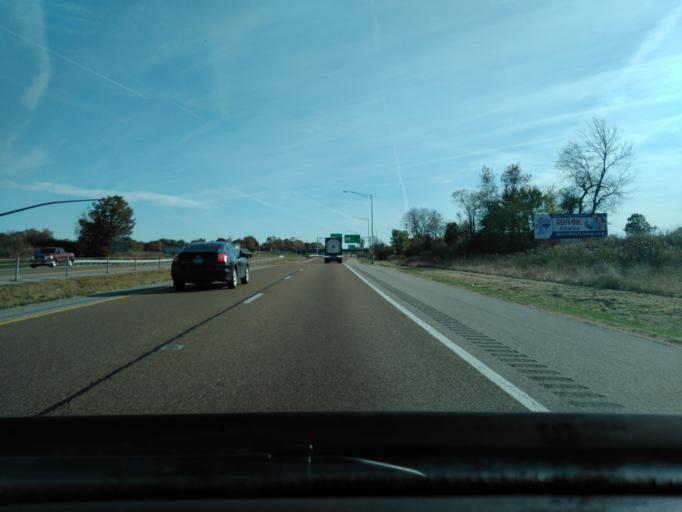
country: US
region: Illinois
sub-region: Madison County
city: Maryville
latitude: 38.7071
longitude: -89.9646
